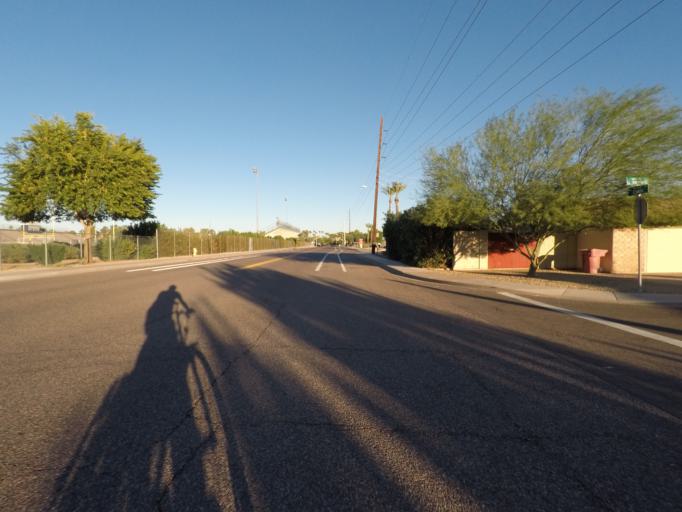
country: US
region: Arizona
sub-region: Maricopa County
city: Scottsdale
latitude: 33.4730
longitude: -111.9200
